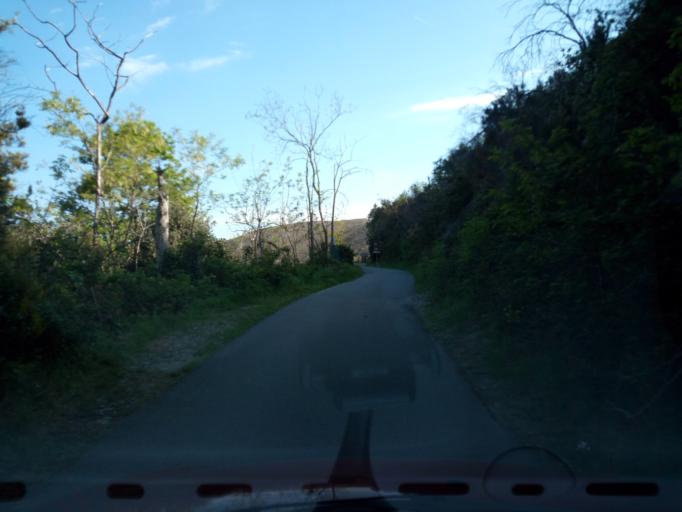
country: IT
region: Liguria
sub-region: Provincia di Genova
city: Sciarborasca
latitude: 44.3983
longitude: 8.6024
